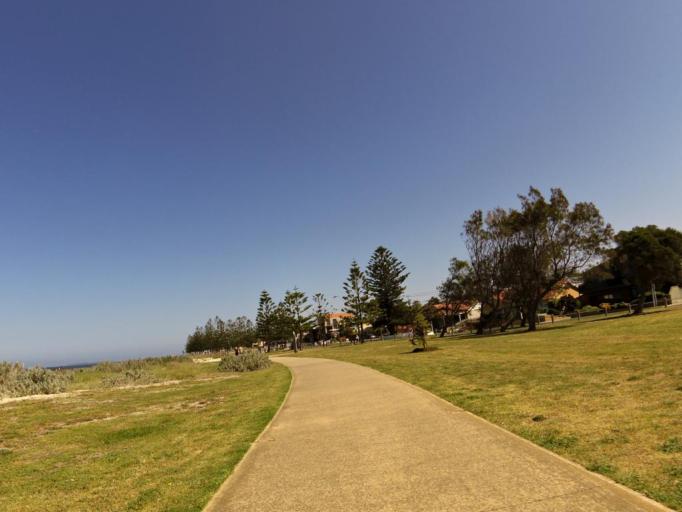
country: AU
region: Victoria
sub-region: Hobsons Bay
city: Seaholme
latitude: -37.8686
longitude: 144.8439
